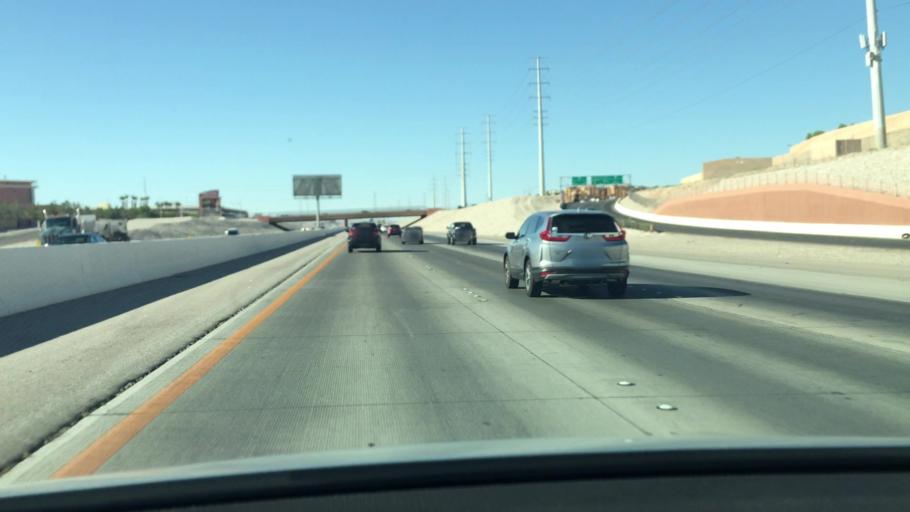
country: US
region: Nevada
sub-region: Clark County
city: Summerlin South
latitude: 36.1632
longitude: -115.3375
